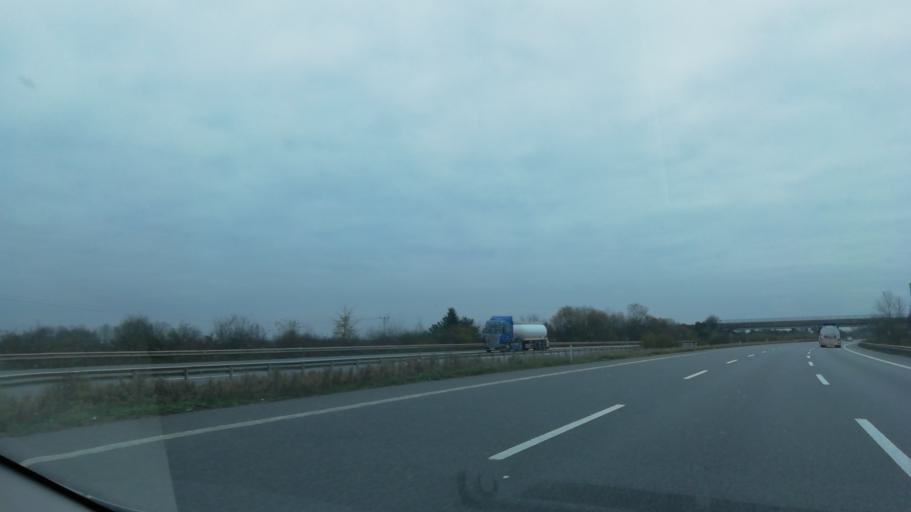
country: TR
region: Duzce
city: Cilimli
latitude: 40.8437
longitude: 31.0192
